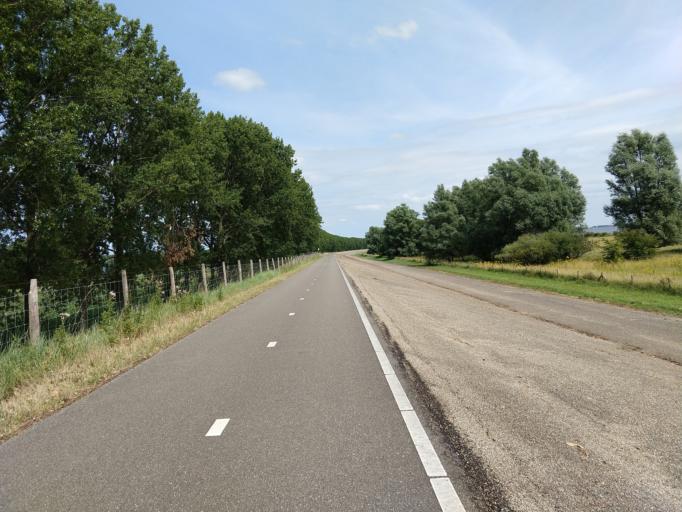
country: NL
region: North Brabant
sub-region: Gemeente Steenbergen
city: Steenbergen
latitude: 51.6582
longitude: 4.2852
